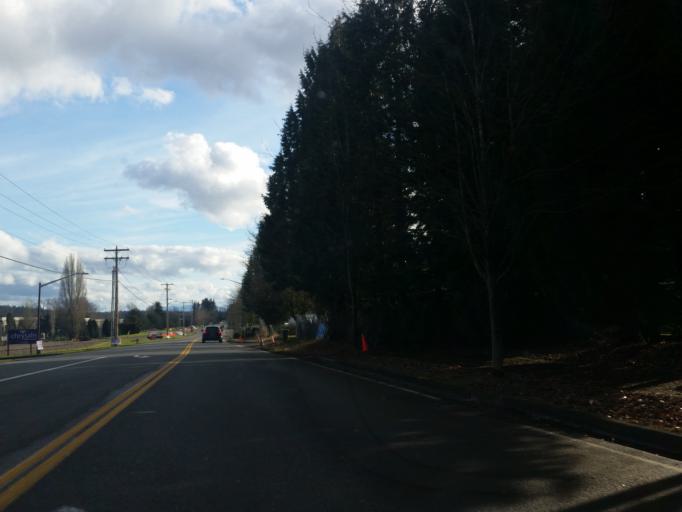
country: US
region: Washington
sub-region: King County
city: Woodinville
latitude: 47.7440
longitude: -122.1603
